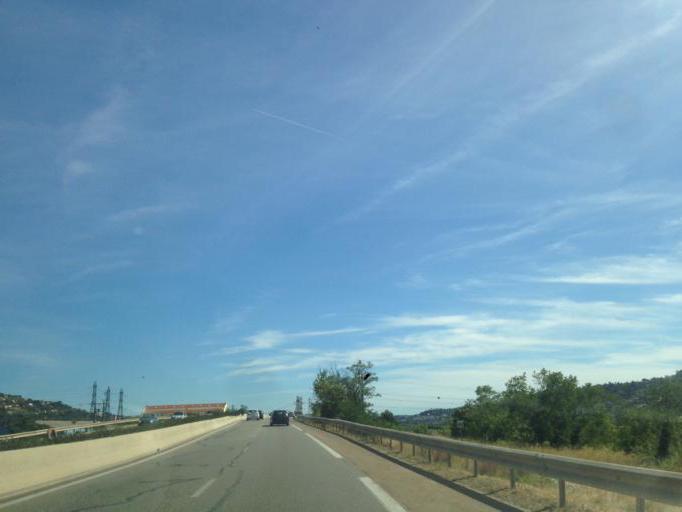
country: FR
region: Provence-Alpes-Cote d'Azur
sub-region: Departement des Alpes-Maritimes
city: La Gaude
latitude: 43.7242
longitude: 7.1858
